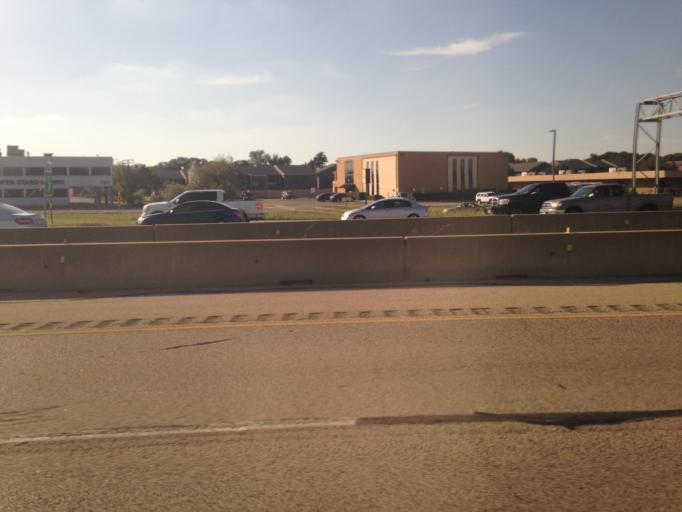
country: US
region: Texas
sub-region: Tarrant County
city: Richland Hills
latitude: 32.8113
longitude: -97.2088
